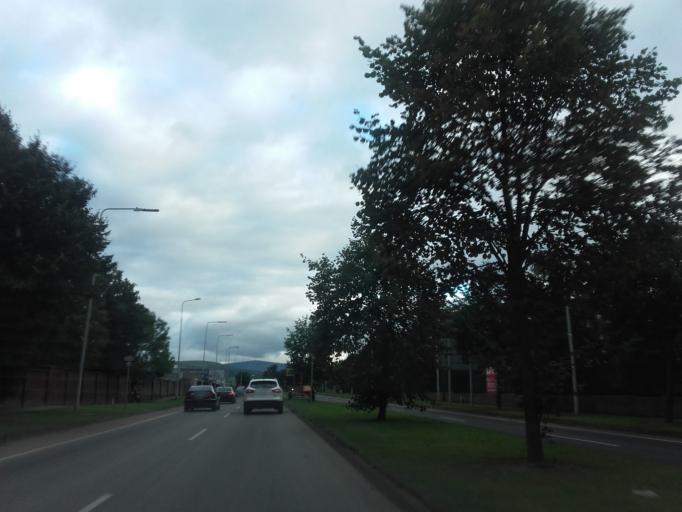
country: IE
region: Leinster
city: Tallaght
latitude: 53.2924
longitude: -6.3687
